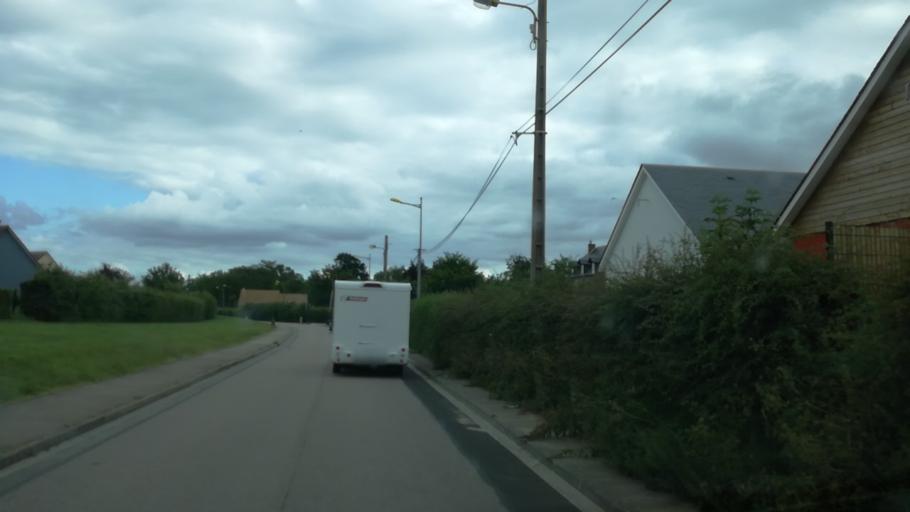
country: FR
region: Haute-Normandie
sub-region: Departement de l'Eure
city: Bourg-Achard
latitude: 49.3485
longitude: 0.8172
